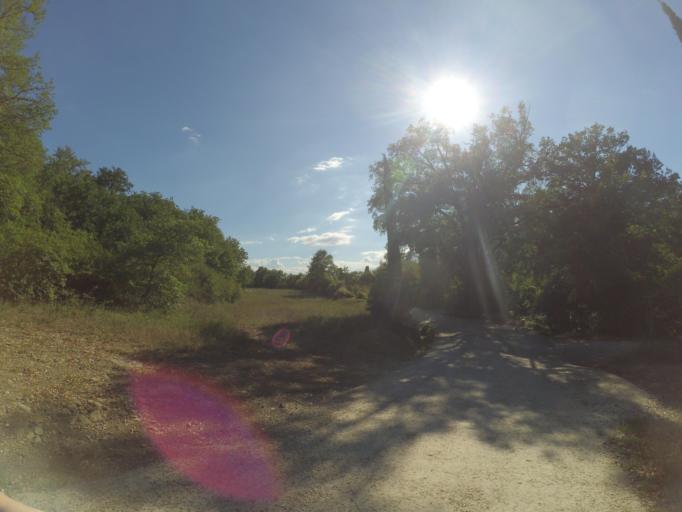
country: IT
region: Tuscany
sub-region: Province of Arezzo
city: Castiglion Fibocchi
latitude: 43.5388
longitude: 11.7680
